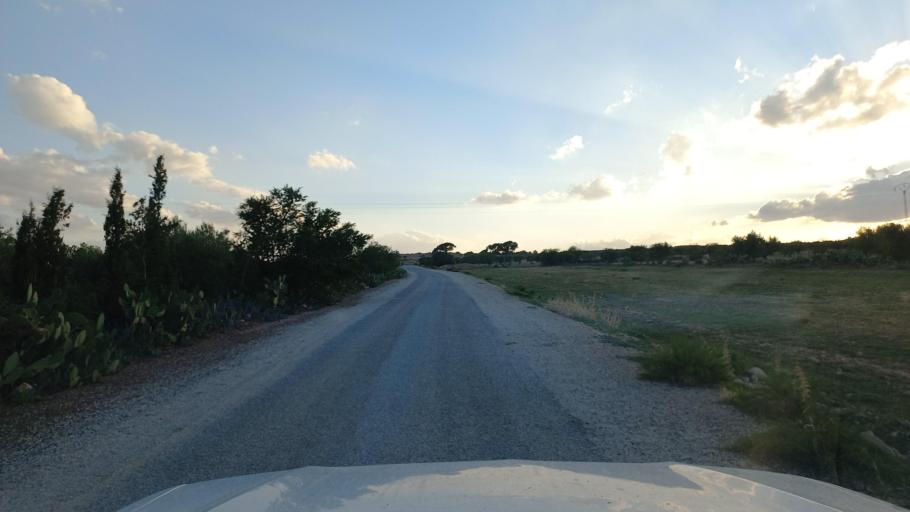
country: TN
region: Al Qasrayn
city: Sbiba
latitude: 35.3764
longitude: 9.0643
